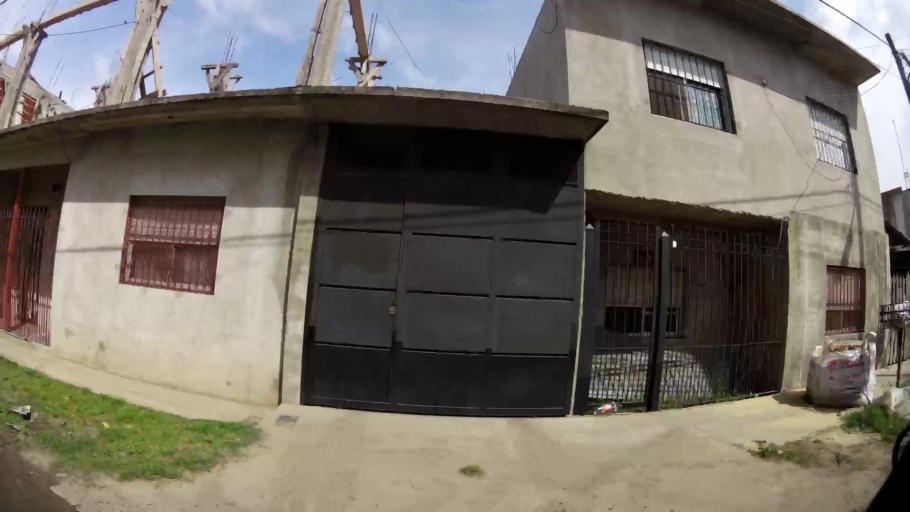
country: AR
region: Buenos Aires
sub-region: Partido de Quilmes
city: Quilmes
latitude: -34.7588
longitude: -58.2525
